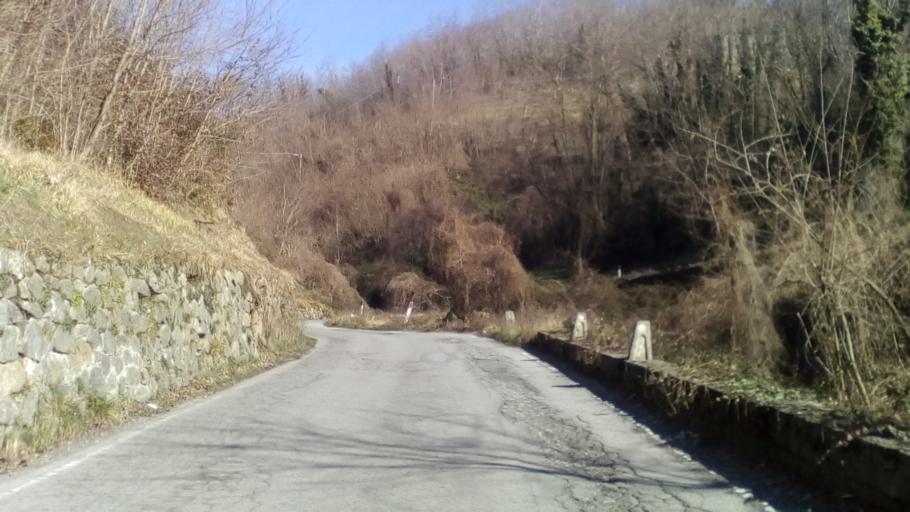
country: IT
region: Tuscany
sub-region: Provincia di Lucca
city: Castiglione di Garfagnana
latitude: 44.1397
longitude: 10.4267
